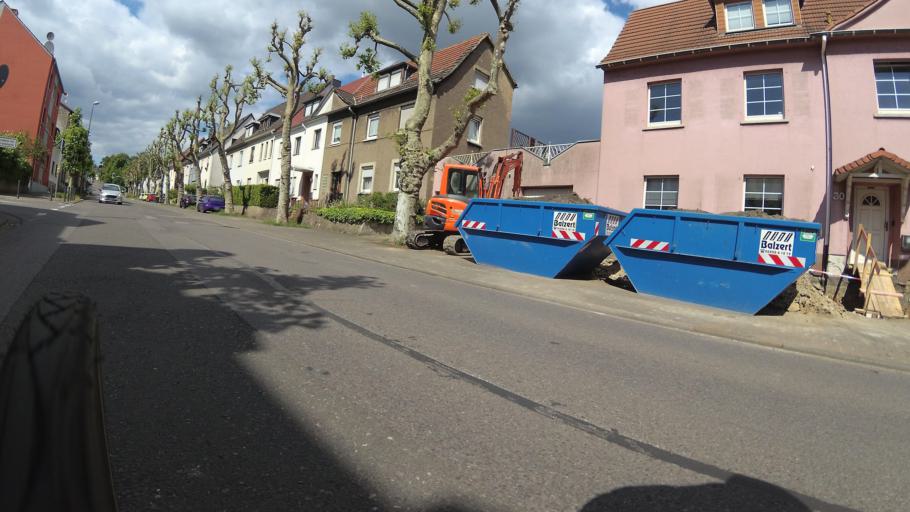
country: DE
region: Saarland
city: Volklingen
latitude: 49.2557
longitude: 6.8570
